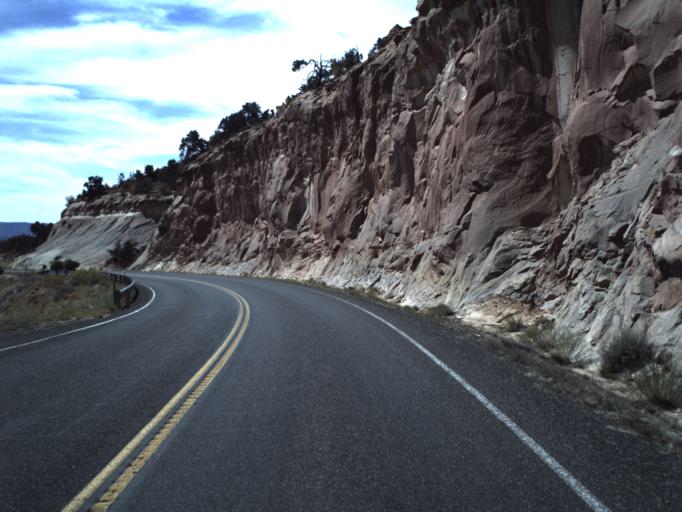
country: US
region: Utah
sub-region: Wayne County
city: Loa
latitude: 37.7454
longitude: -111.4546
